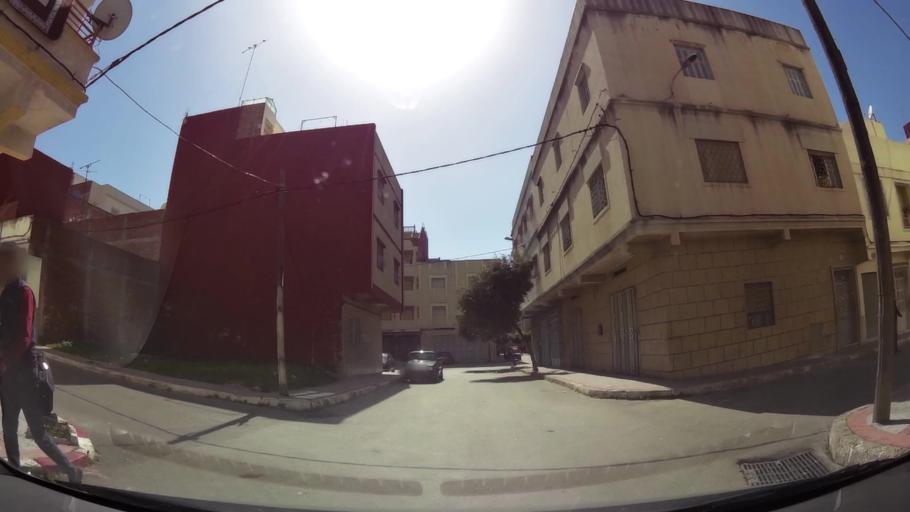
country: MA
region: Tanger-Tetouan
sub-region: Tanger-Assilah
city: Tangier
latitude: 35.7489
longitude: -5.8098
